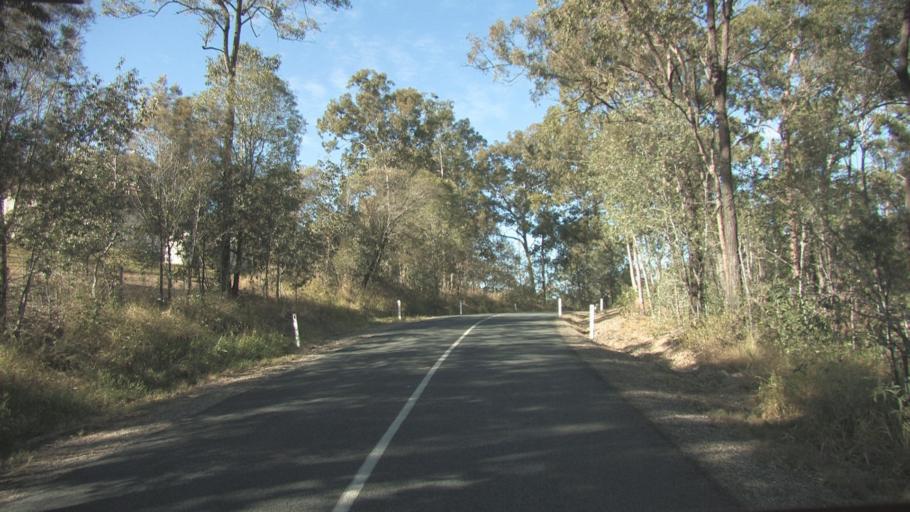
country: AU
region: Queensland
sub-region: Logan
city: Windaroo
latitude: -27.8164
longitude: 153.1685
